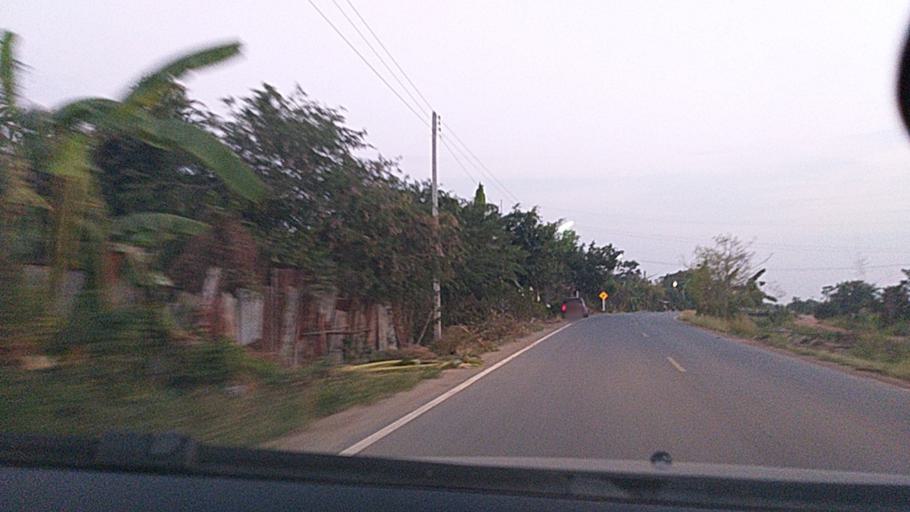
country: TH
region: Sing Buri
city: Phrom Buri
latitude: 14.8252
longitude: 100.4071
